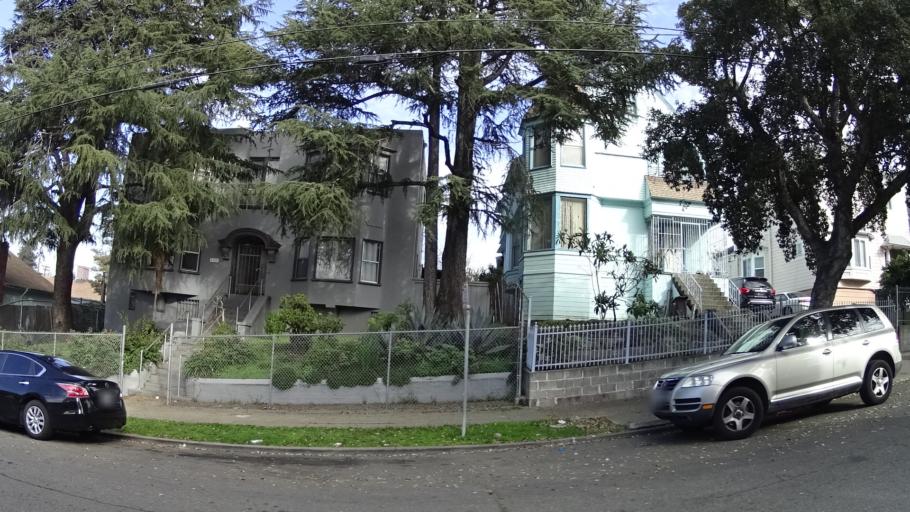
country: US
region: California
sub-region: Alameda County
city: Alameda
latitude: 37.7862
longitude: -122.2320
